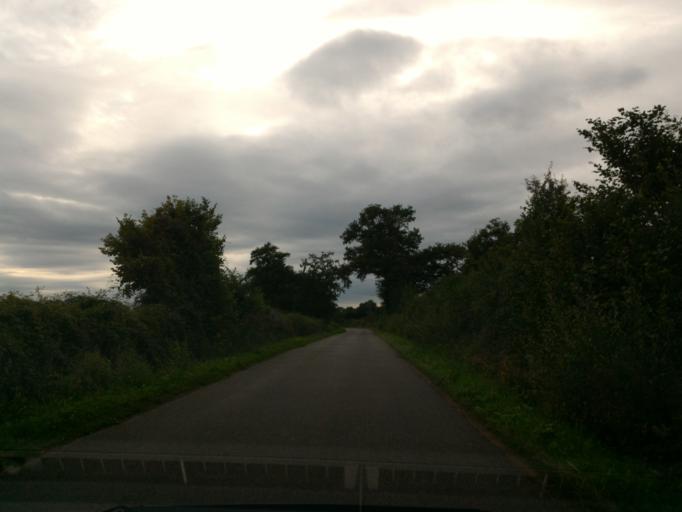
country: FR
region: Poitou-Charentes
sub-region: Departement de la Charente
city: Brigueuil
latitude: 45.9331
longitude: 0.8185
